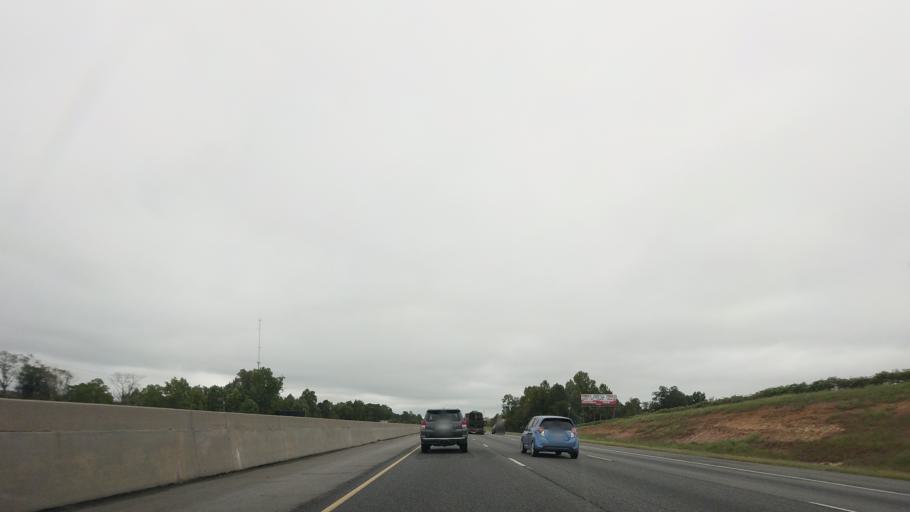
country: US
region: Georgia
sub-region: Turner County
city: Ashburn
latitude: 31.7452
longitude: -83.6590
